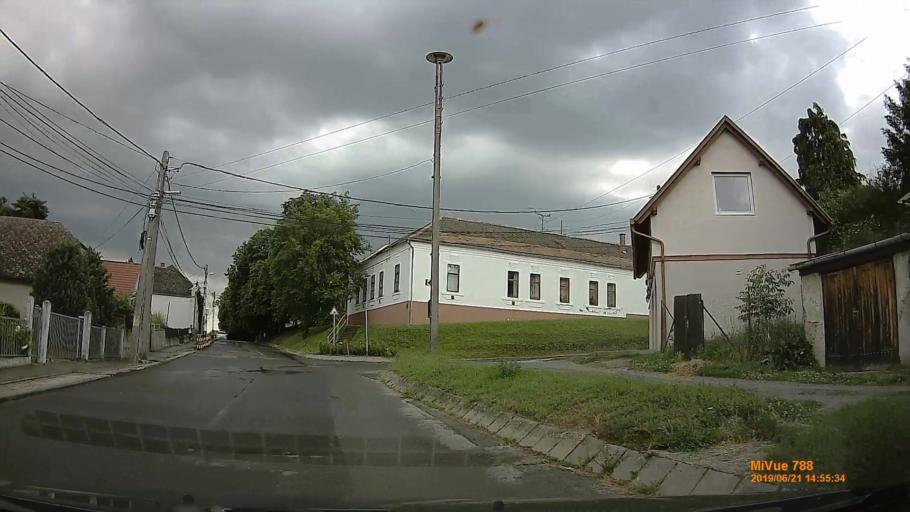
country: HU
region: Baranya
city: Hosszuheteny
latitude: 46.1221
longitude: 18.3105
